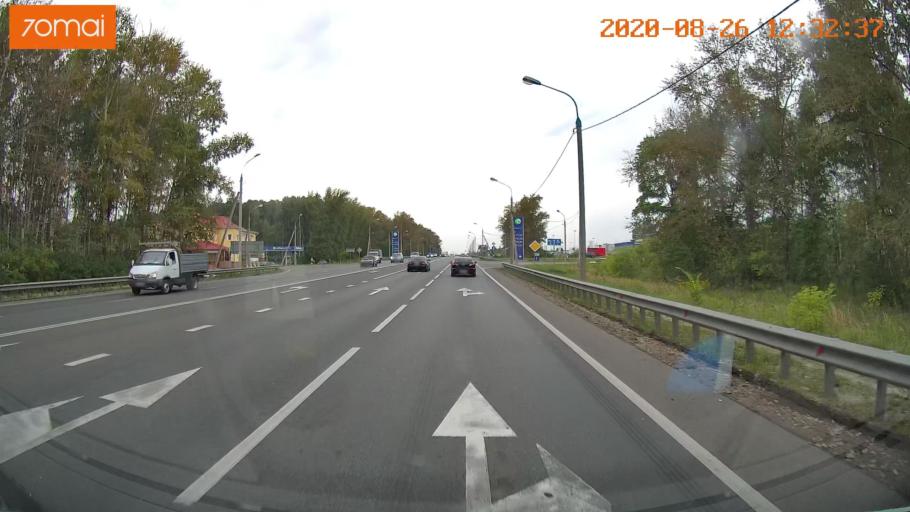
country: RU
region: Rjazan
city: Ryazan'
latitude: 54.5783
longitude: 39.7874
